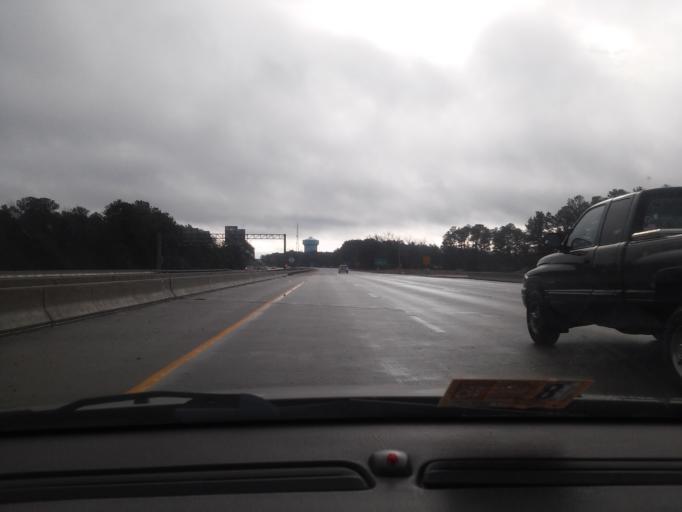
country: US
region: Virginia
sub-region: Henrico County
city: Short Pump
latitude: 37.6485
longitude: -77.5943
